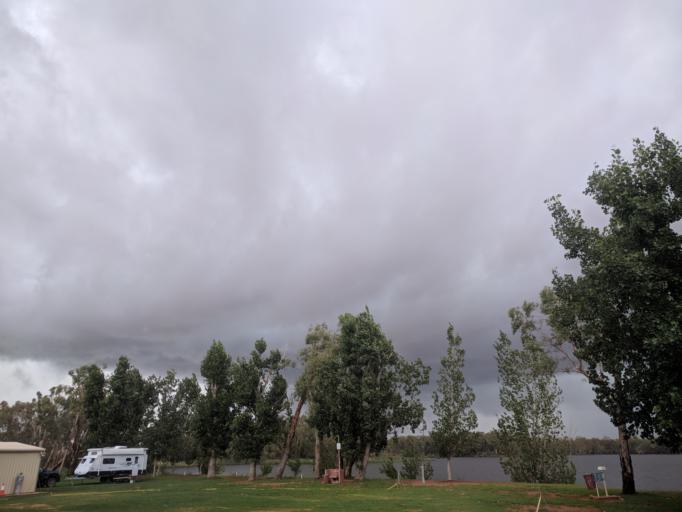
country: AU
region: New South Wales
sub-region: Broken Hill Municipality
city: Broken Hill
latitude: -32.2681
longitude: 142.3856
